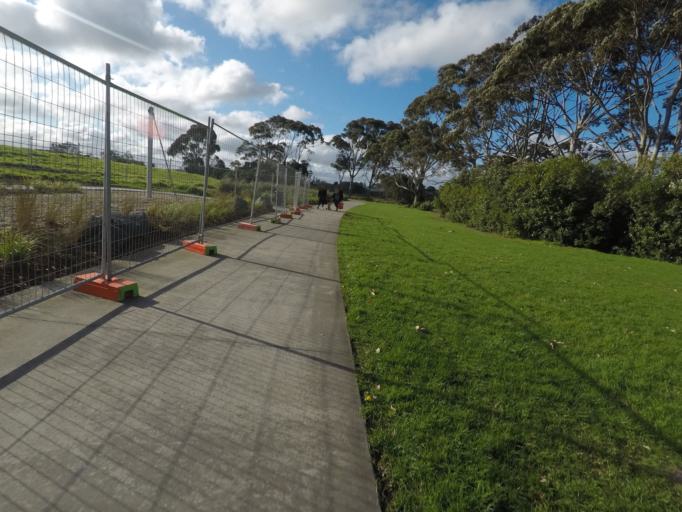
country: NZ
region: Auckland
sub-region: Auckland
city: Rosebank
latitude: -36.8937
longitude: 174.6714
